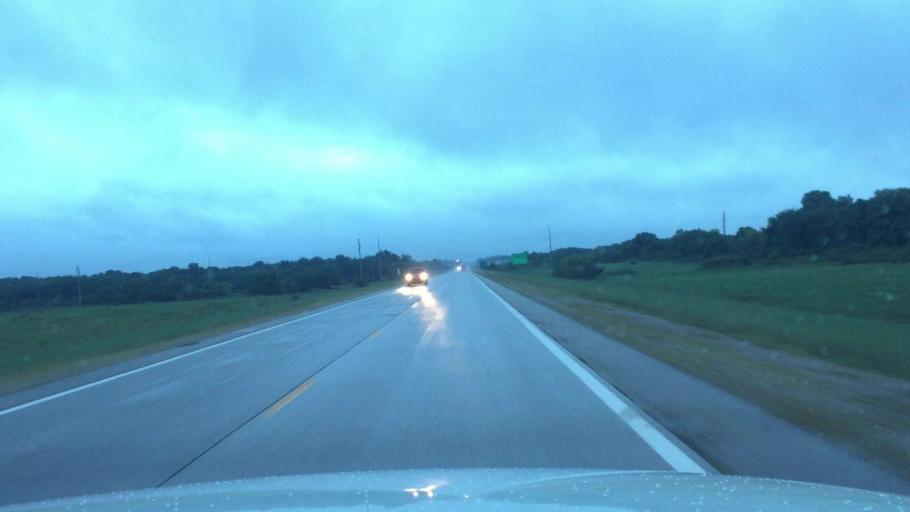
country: US
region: Kansas
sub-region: Neosho County
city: Chanute
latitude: 37.7081
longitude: -95.4796
